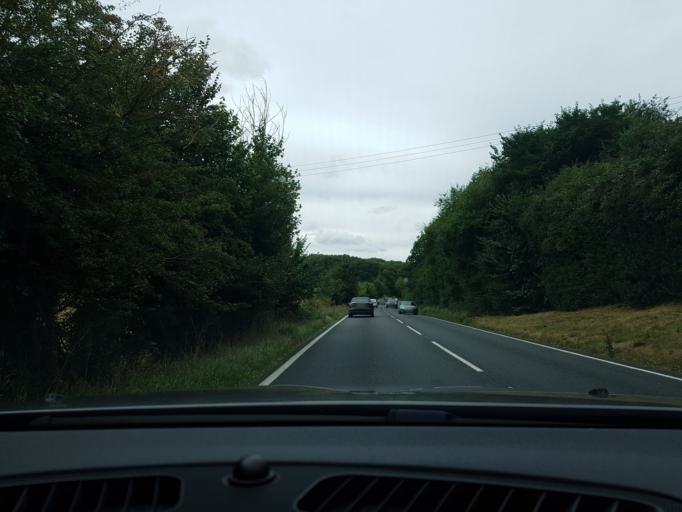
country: GB
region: England
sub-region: Hampshire
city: Kingsclere
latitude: 51.3211
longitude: -1.2170
